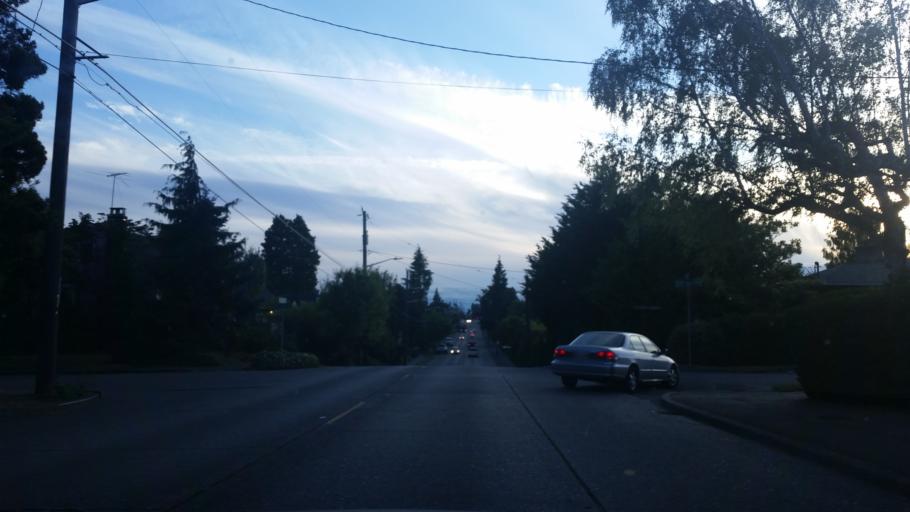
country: US
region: Washington
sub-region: King County
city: Shoreline
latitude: 47.6906
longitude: -122.3828
